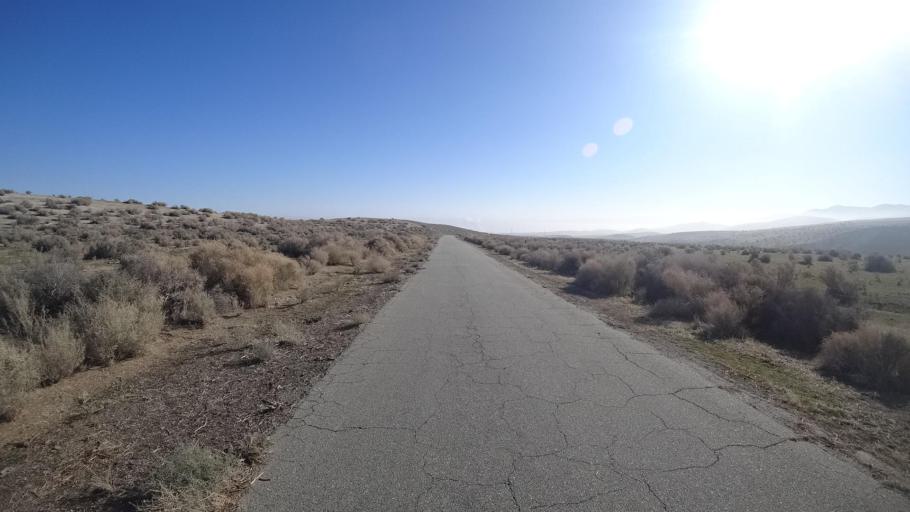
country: US
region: California
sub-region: Kern County
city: Taft Heights
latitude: 35.2312
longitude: -119.6485
